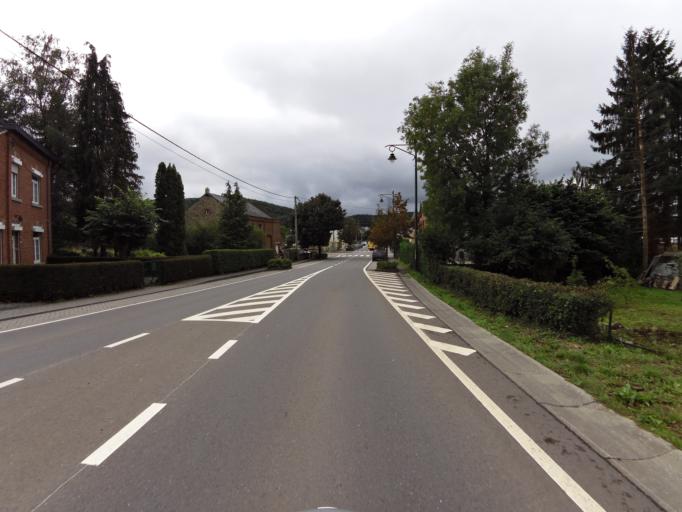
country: BE
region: Wallonia
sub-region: Province de Namur
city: Rochefort
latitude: 50.1285
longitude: 5.1904
